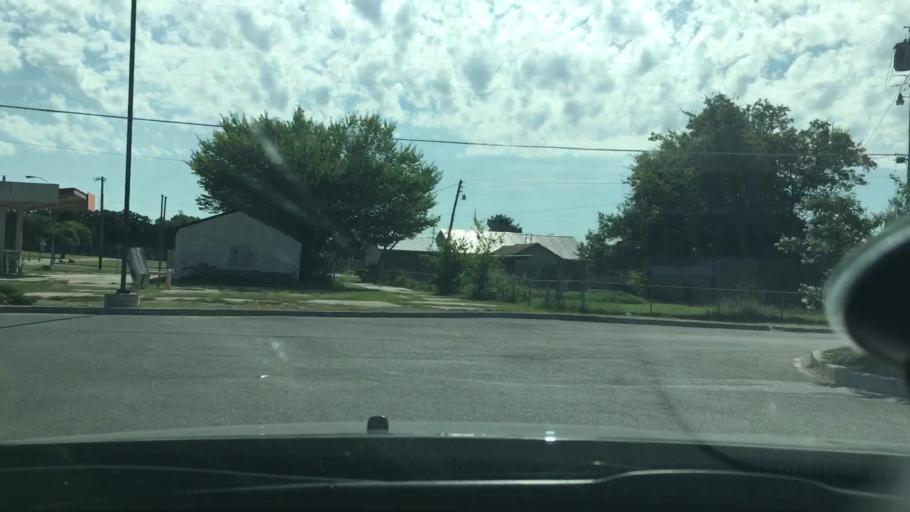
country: US
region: Oklahoma
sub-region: Carter County
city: Ardmore
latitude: 34.1628
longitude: -97.1226
